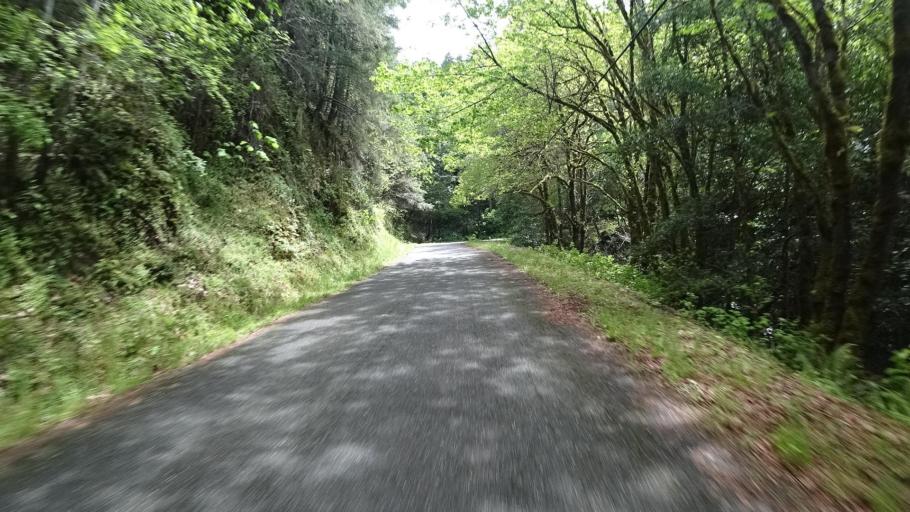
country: US
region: California
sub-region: Humboldt County
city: Blue Lake
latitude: 40.7608
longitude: -123.9036
